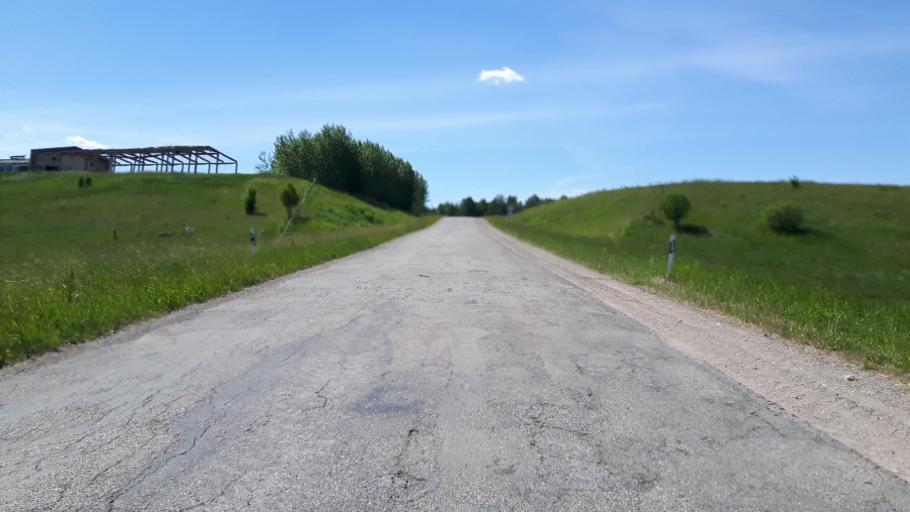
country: LV
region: Kandava
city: Kandava
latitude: 57.0361
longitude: 22.8924
